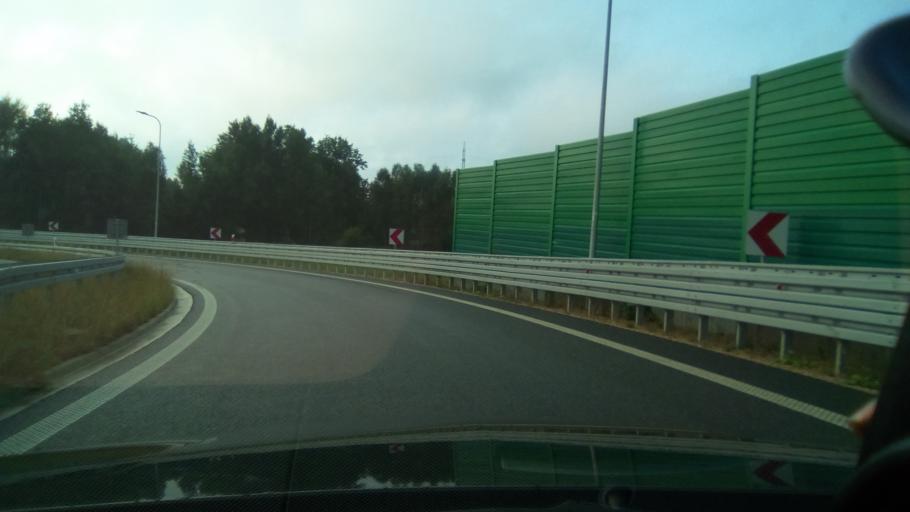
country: PL
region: Silesian Voivodeship
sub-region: Powiat czestochowski
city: Konopiska
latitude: 50.7439
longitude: 19.0435
